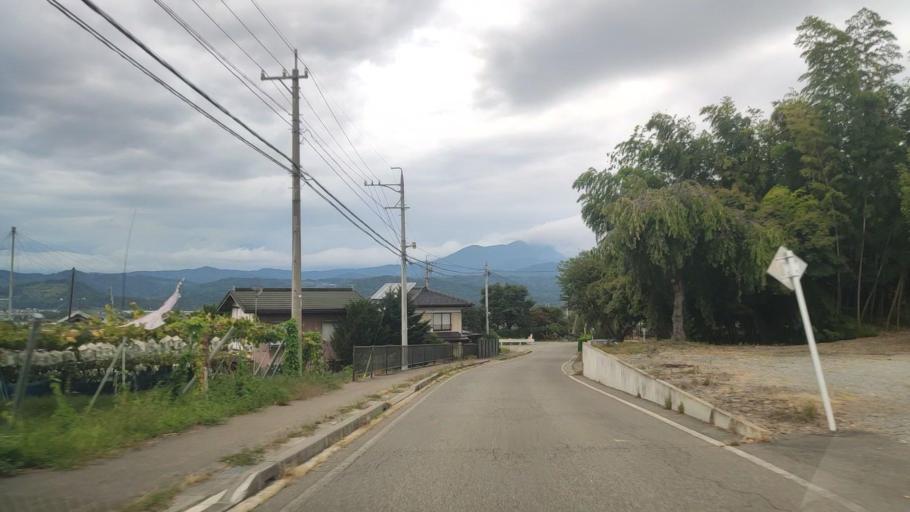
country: JP
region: Nagano
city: Nakano
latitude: 36.7757
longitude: 138.3763
